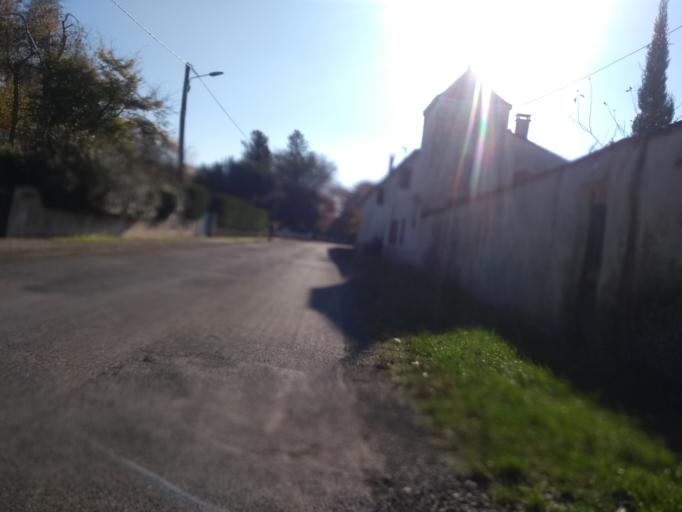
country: FR
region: Aquitaine
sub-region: Departement de la Gironde
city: Leognan
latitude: 44.7377
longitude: -0.5999
